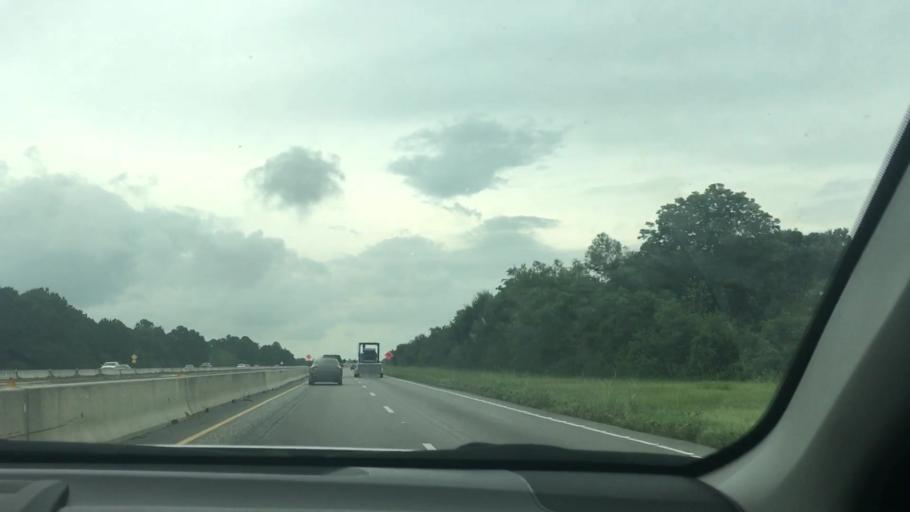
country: US
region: Texas
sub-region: Chambers County
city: Winnie
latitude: 29.8688
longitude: -94.3453
